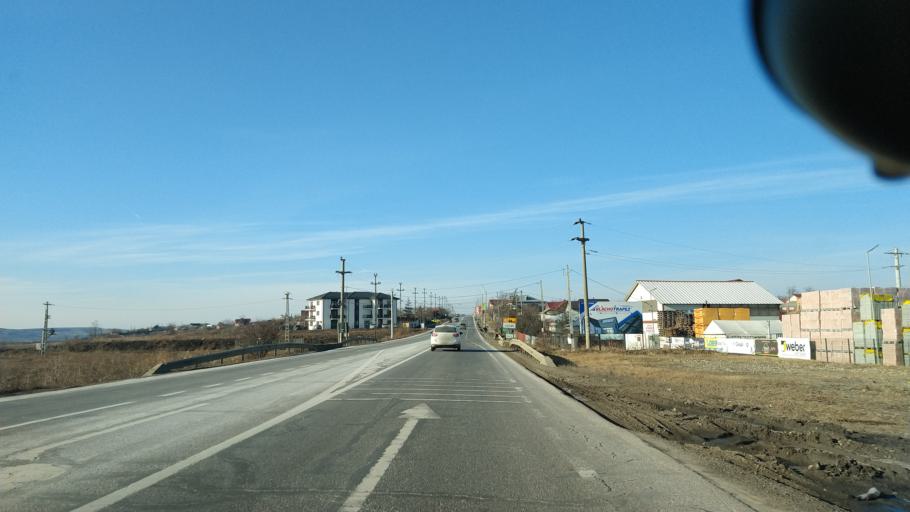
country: RO
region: Iasi
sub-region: Comuna Letcani
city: Letcani
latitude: 47.1906
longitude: 27.4291
